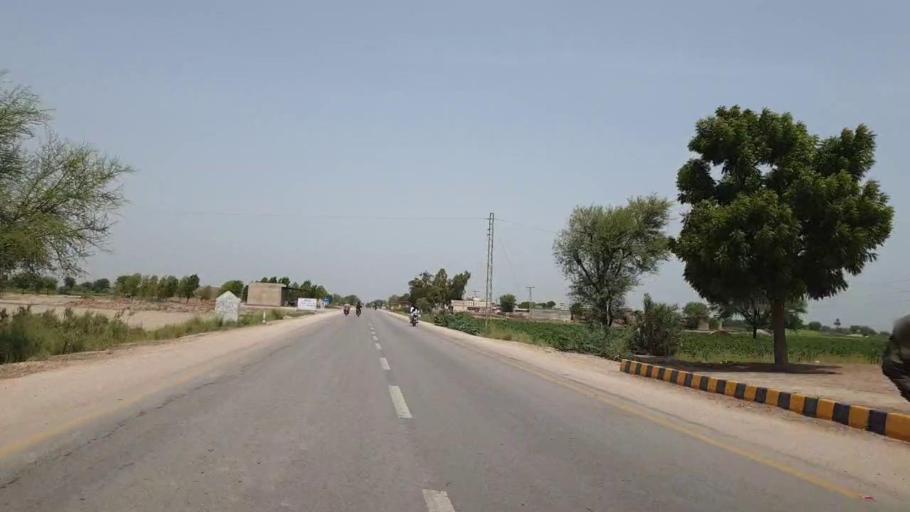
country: PK
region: Sindh
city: Shahpur Chakar
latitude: 26.1678
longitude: 68.6223
